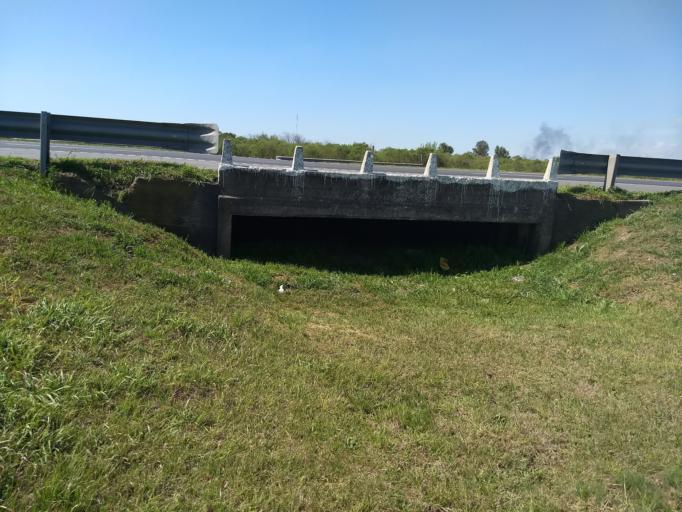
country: AR
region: Santa Fe
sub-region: Departamento de San Lorenzo
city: San Lorenzo
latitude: -32.7055
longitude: -60.7765
